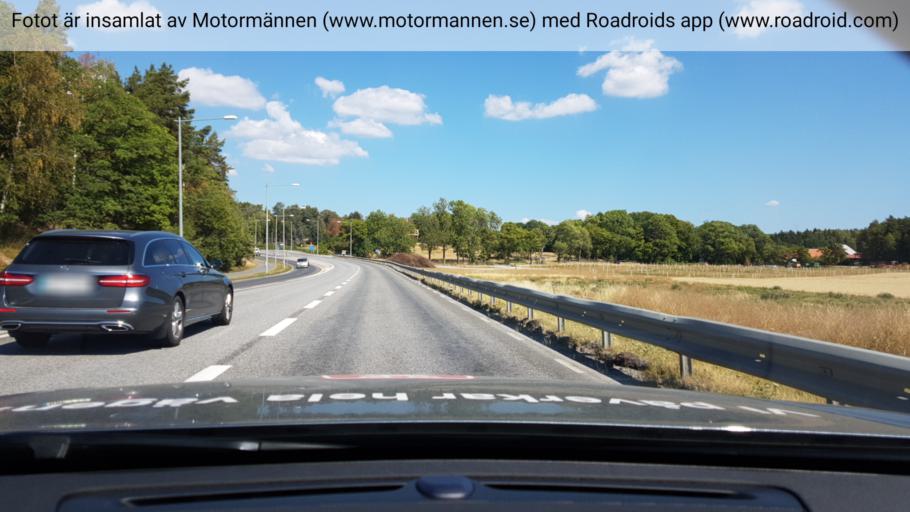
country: SE
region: Stockholm
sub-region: Ekero Kommun
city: Ekeroe
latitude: 59.3077
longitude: 17.8596
